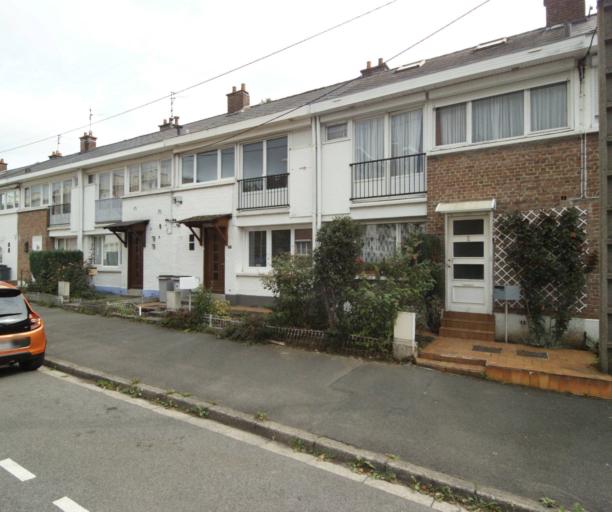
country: FR
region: Nord-Pas-de-Calais
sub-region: Departement du Nord
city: Lambersart
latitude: 50.6540
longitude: 3.0375
